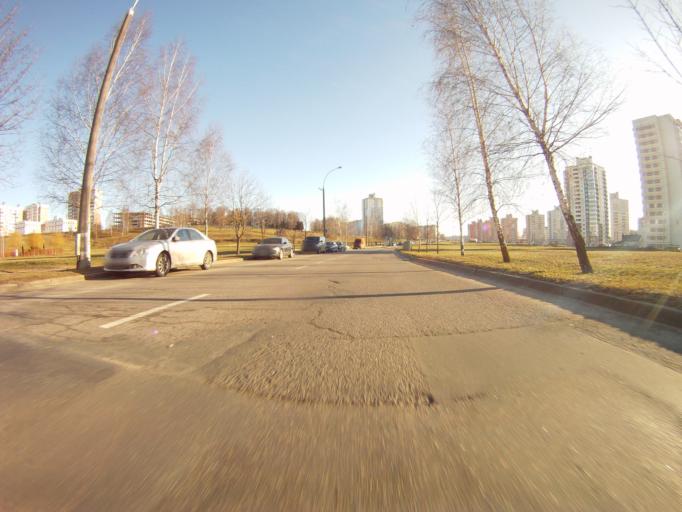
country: BY
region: Minsk
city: Novoye Medvezhino
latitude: 53.8796
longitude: 27.4443
